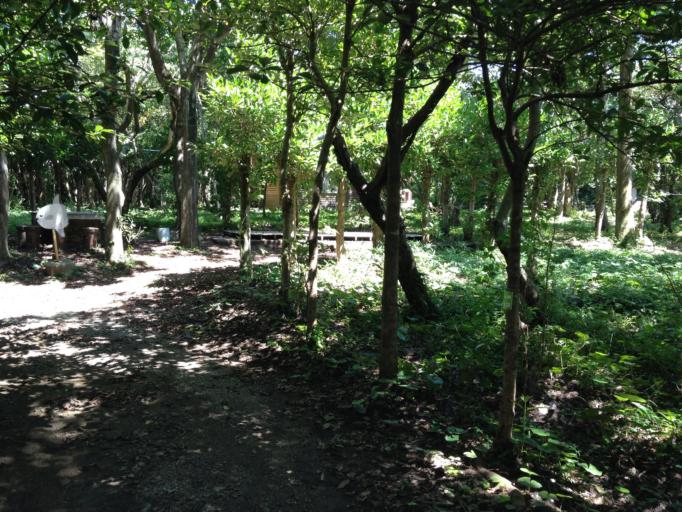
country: JP
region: Wakayama
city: Shingu
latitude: 33.4457
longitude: 135.7815
